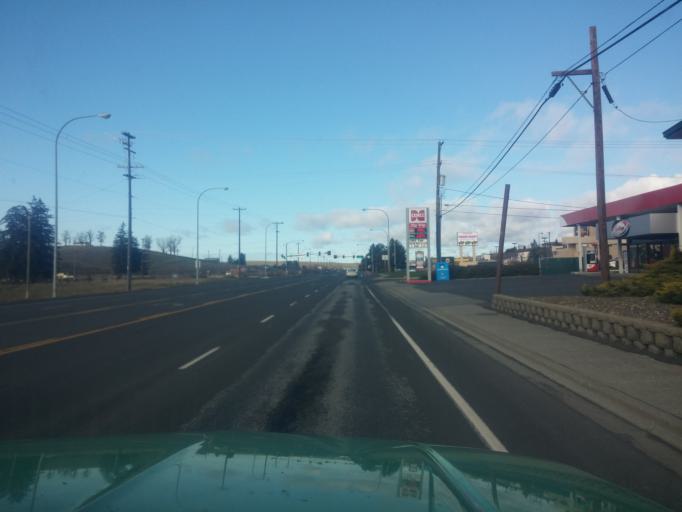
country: US
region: Idaho
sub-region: Latah County
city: Moscow
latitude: 46.7327
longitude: -117.0220
